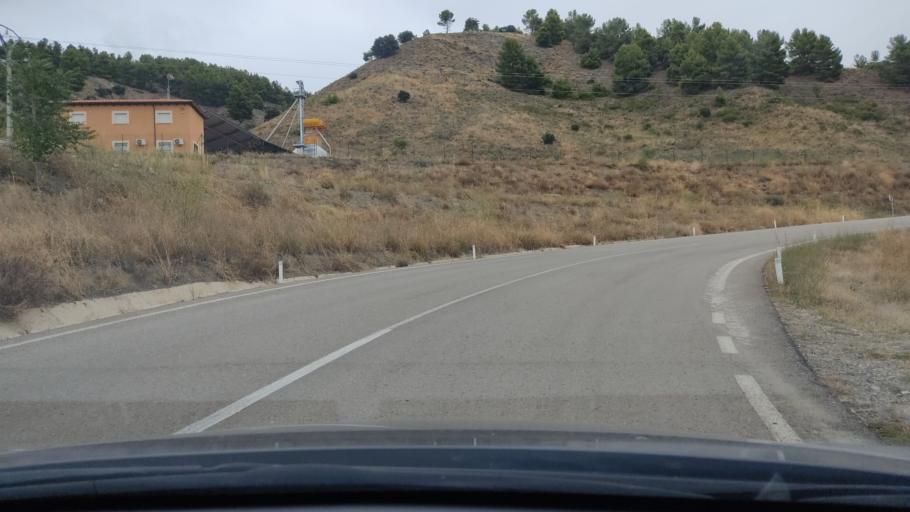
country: ES
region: Aragon
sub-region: Provincia de Teruel
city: Burbaguena
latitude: 41.0271
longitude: -1.3431
